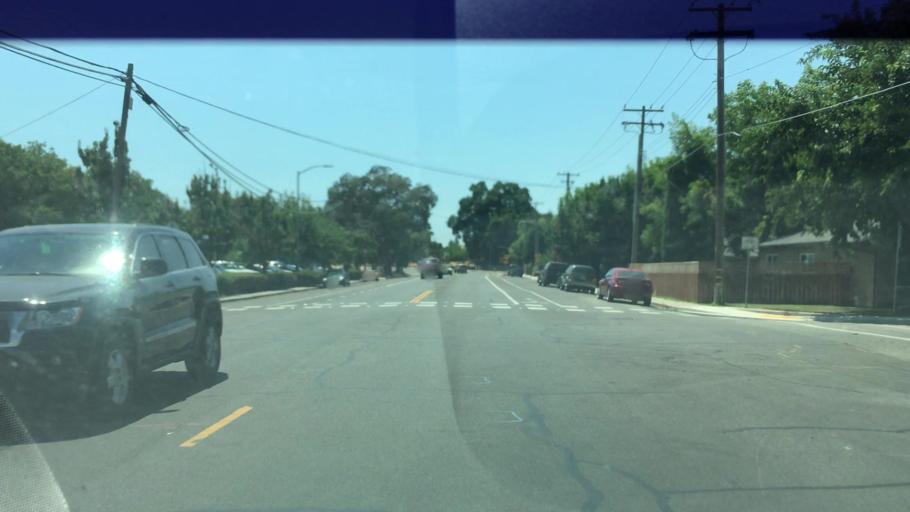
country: US
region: California
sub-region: Sacramento County
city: Galt
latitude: 38.2485
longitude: -121.3072
